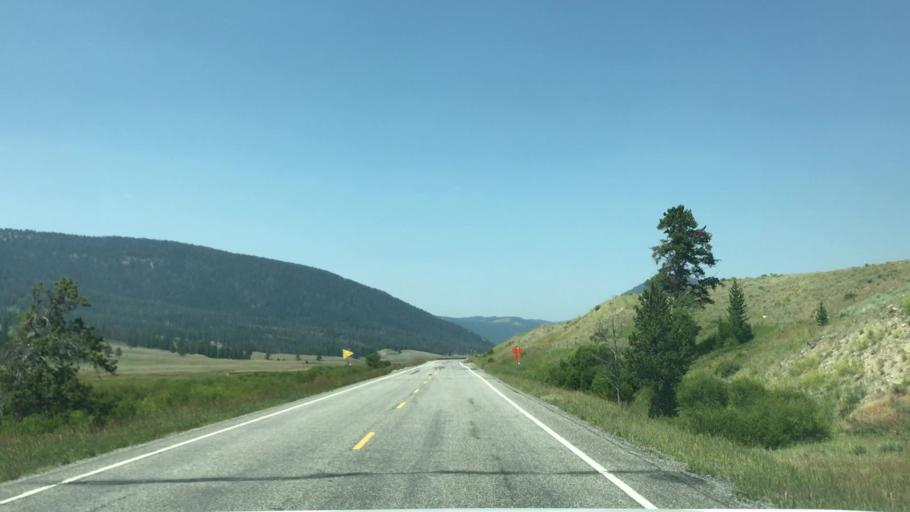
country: US
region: Montana
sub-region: Gallatin County
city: Big Sky
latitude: 45.0416
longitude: -111.1257
